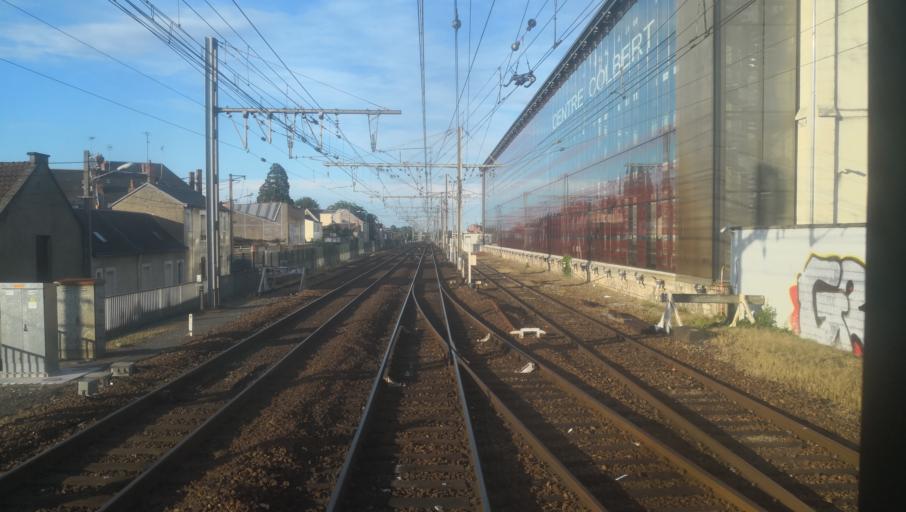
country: FR
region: Centre
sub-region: Departement de l'Indre
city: Chateauroux
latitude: 46.8107
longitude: 1.7023
